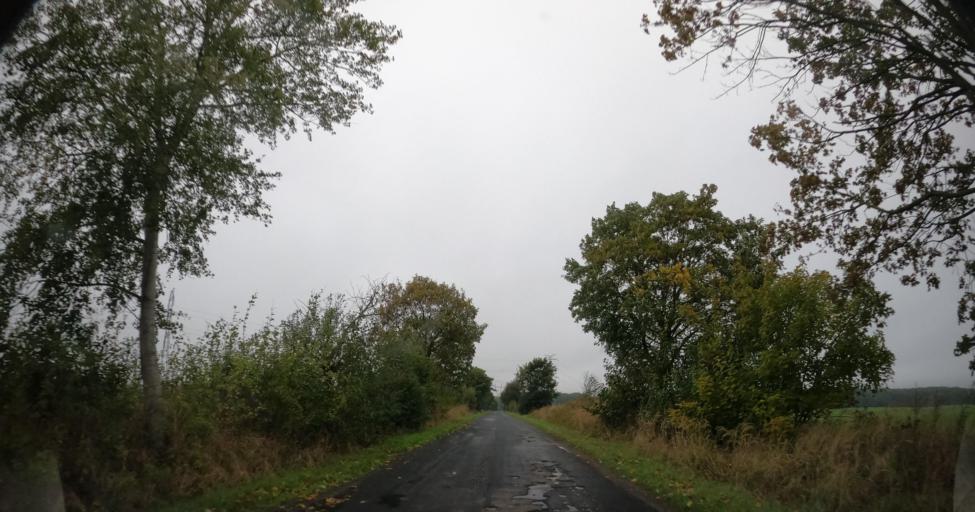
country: PL
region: West Pomeranian Voivodeship
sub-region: Powiat pyrzycki
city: Kozielice
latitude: 53.0500
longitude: 14.7538
